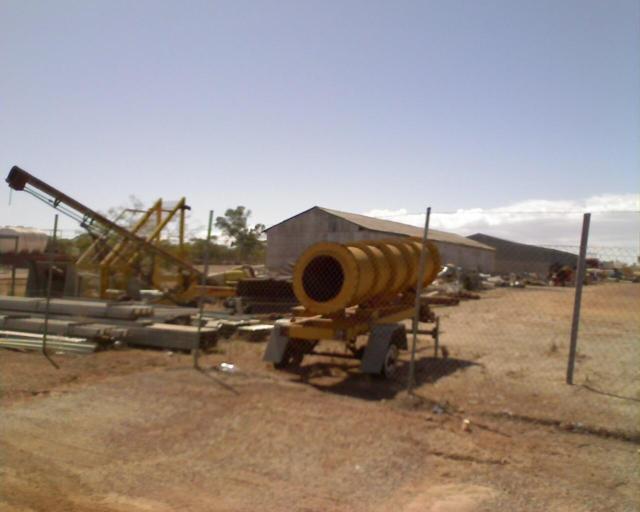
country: AU
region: Western Australia
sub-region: Moora
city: Moora
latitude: -29.8836
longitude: 116.0242
